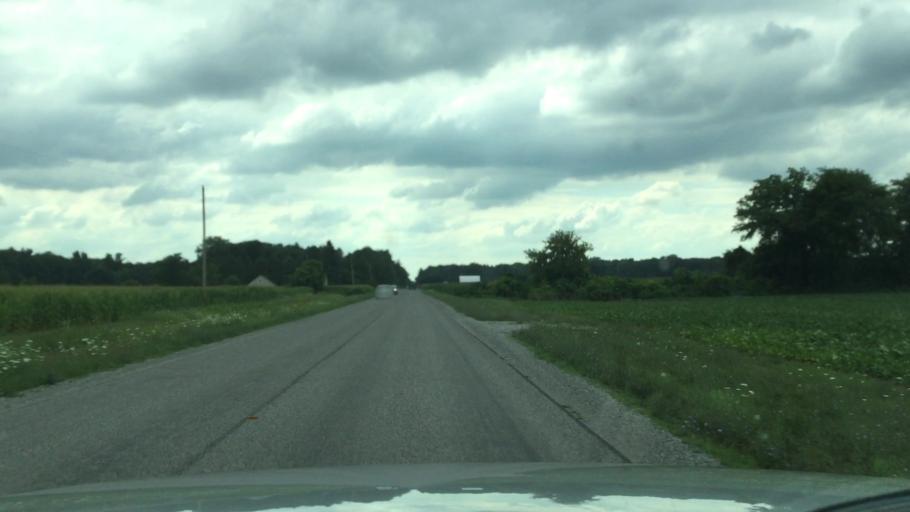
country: US
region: Michigan
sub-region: Saginaw County
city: Frankenmuth
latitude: 43.3217
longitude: -83.7670
